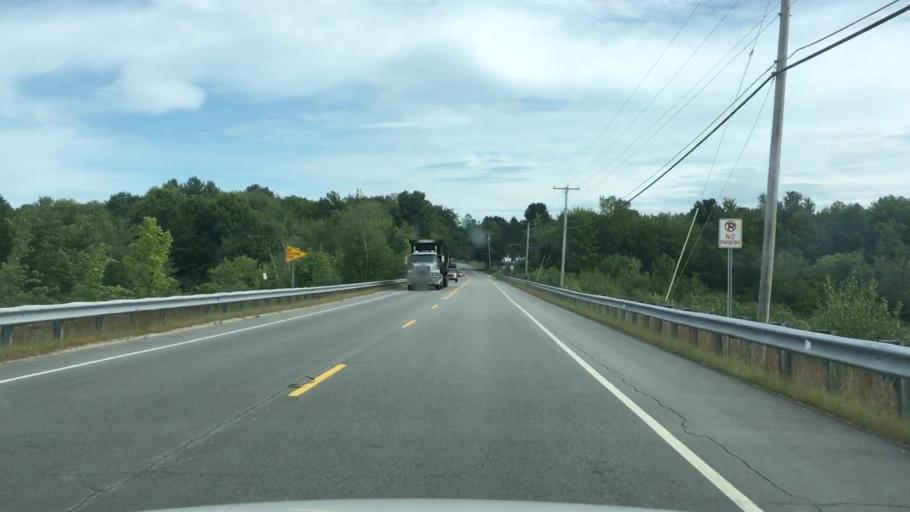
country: US
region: New Hampshire
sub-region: Strafford County
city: Madbury
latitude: 43.1962
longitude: -70.9501
